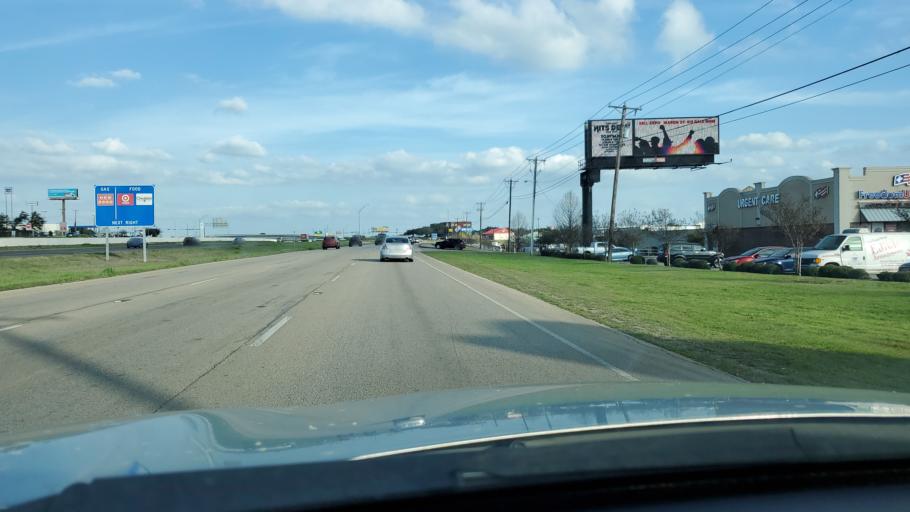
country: US
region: Texas
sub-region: Bell County
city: Harker Heights
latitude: 31.0719
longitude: -97.6759
